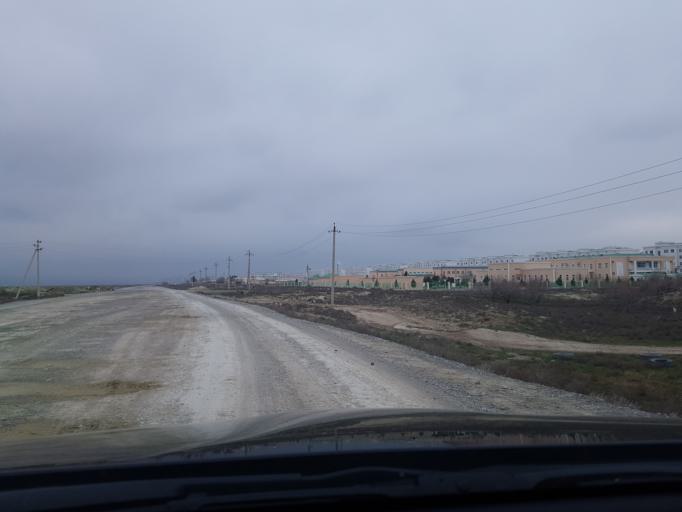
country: TM
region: Ahal
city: Abadan
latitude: 38.1604
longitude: 57.9412
